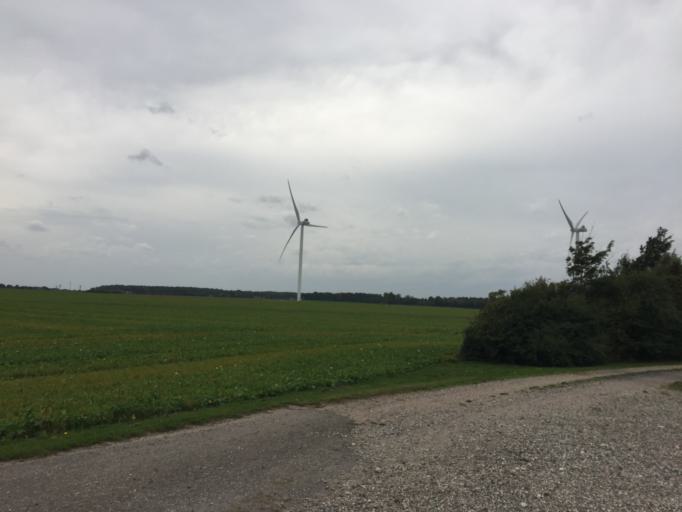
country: DK
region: Zealand
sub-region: Lolland Kommune
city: Maribo
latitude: 54.8106
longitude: 11.5099
